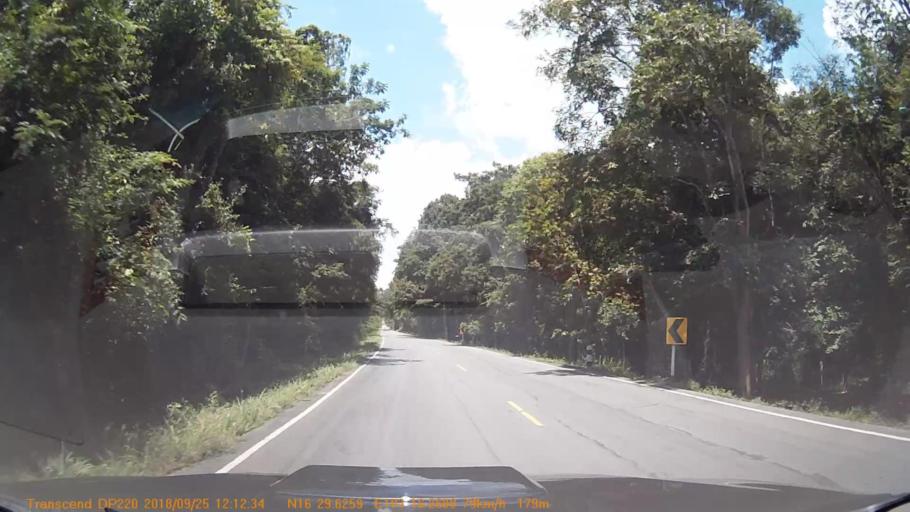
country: TH
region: Kalasin
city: Huai Mek
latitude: 16.4939
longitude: 103.2711
